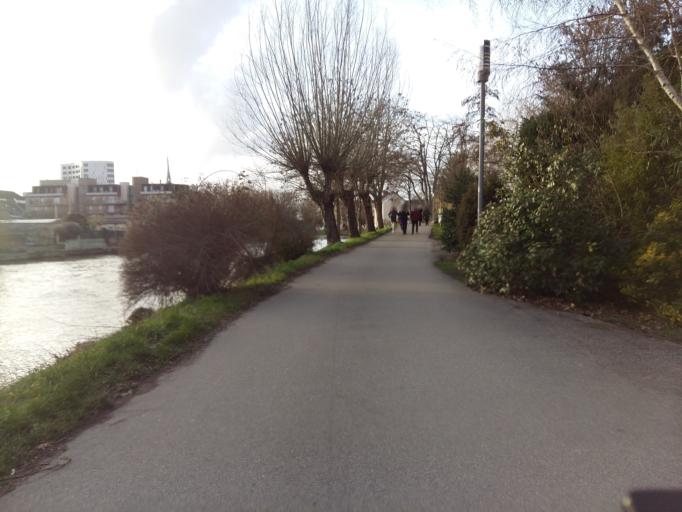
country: FR
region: Picardie
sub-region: Departement de la Somme
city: Rivery
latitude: 49.8944
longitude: 2.3139
